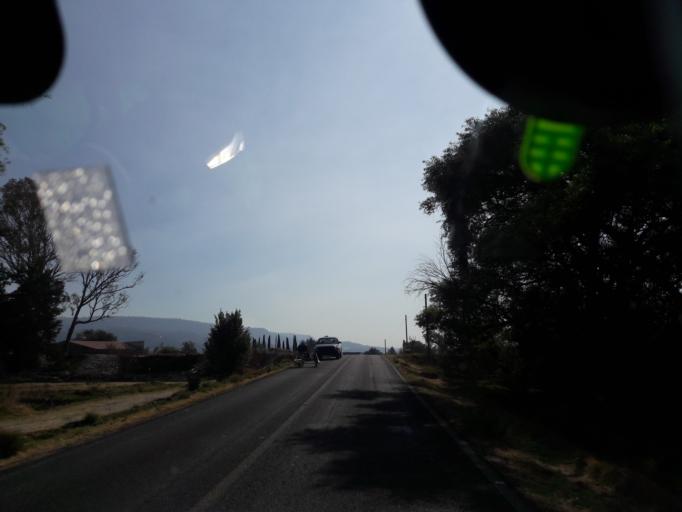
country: MX
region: Tlaxcala
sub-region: Ixtacuixtla de Mariano Matamoros
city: Santa Justina Ecatepec
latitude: 19.3166
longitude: -98.3214
